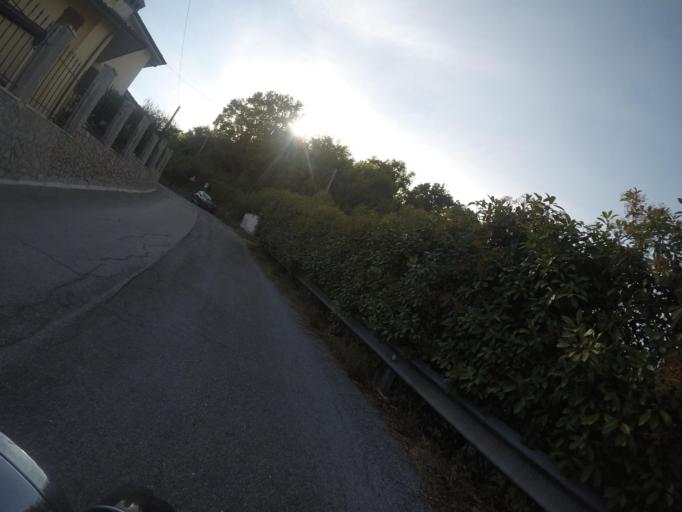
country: IT
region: Tuscany
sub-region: Provincia di Massa-Carrara
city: Carrara
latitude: 44.0877
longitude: 10.0932
